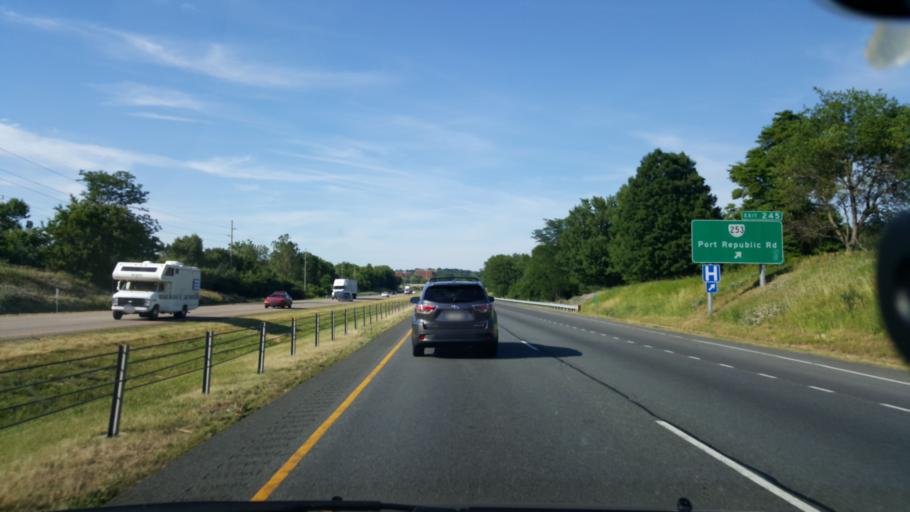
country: US
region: Virginia
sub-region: City of Harrisonburg
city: Harrisonburg
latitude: 38.4232
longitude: -78.8800
